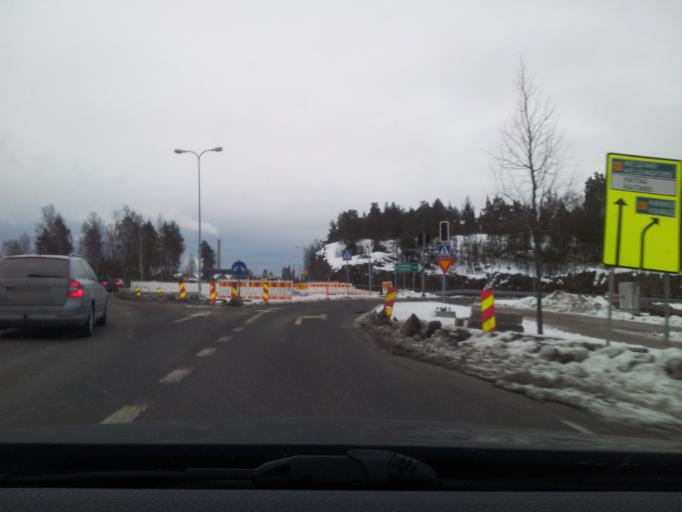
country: FI
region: Uusimaa
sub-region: Helsinki
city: Kauniainen
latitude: 60.1611
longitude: 24.7040
